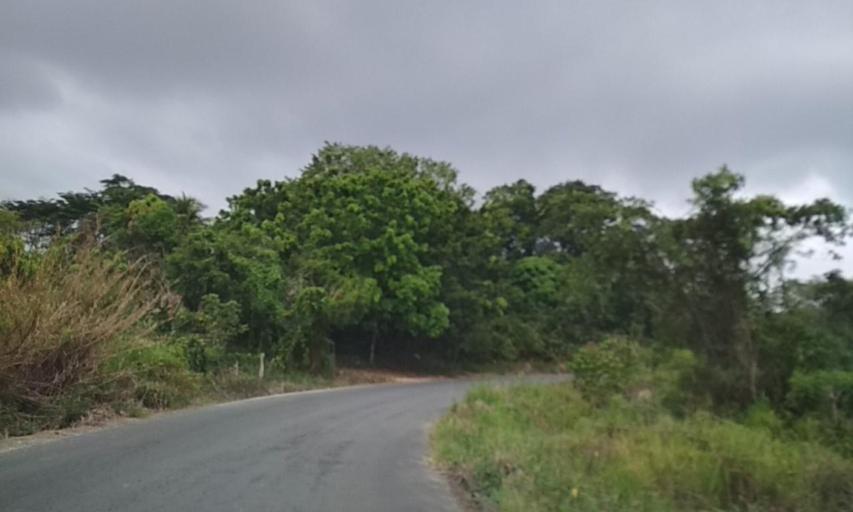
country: MX
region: Tabasco
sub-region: Huimanguillo
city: Francisco Rueda
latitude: 17.6261
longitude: -94.0900
